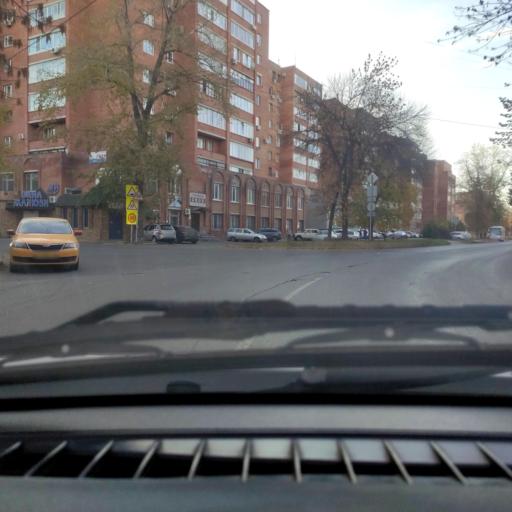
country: RU
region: Samara
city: Tol'yatti
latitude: 53.5093
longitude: 49.4065
